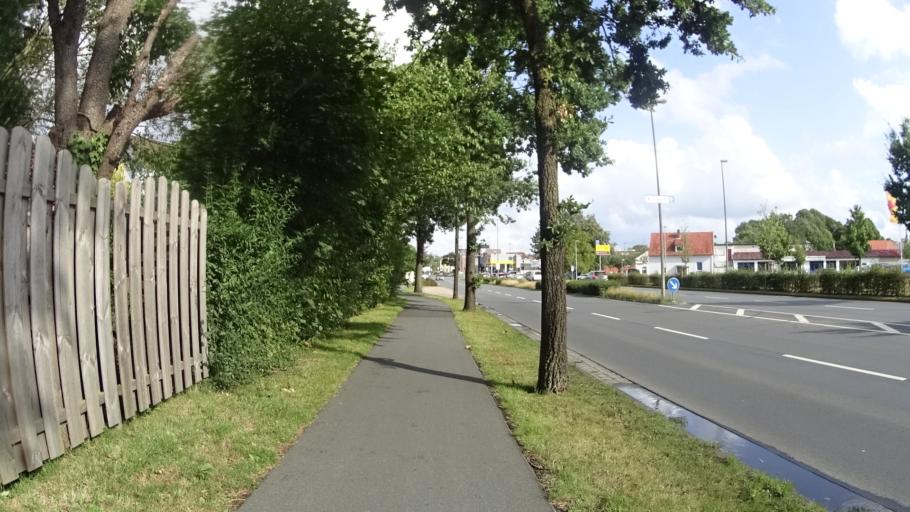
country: DE
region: Lower Saxony
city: Varel
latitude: 53.3955
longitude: 8.1331
